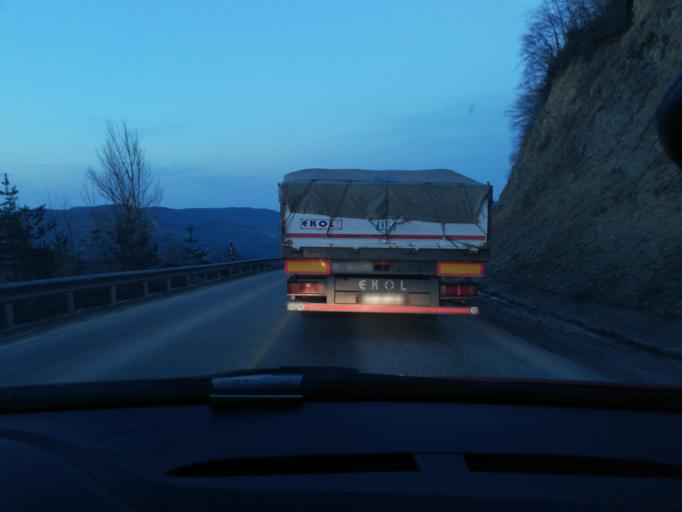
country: TR
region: Kastamonu
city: Inebolu
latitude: 41.9160
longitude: 33.7268
